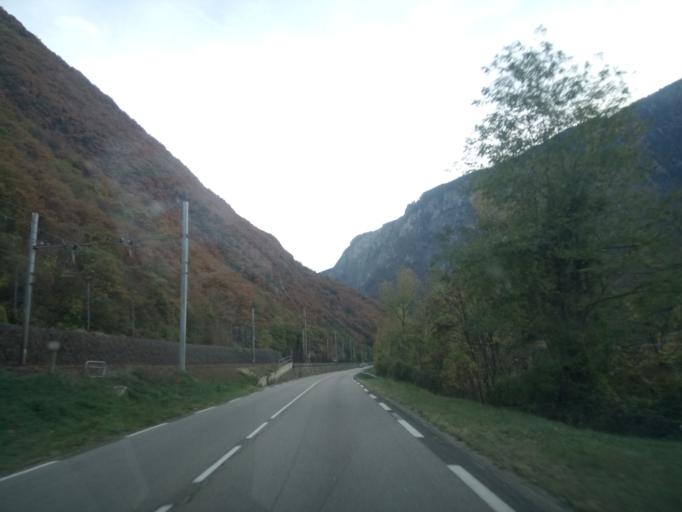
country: FR
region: Rhone-Alpes
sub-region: Departement de la Savoie
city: La Chambre
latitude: 45.3296
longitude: 6.3177
